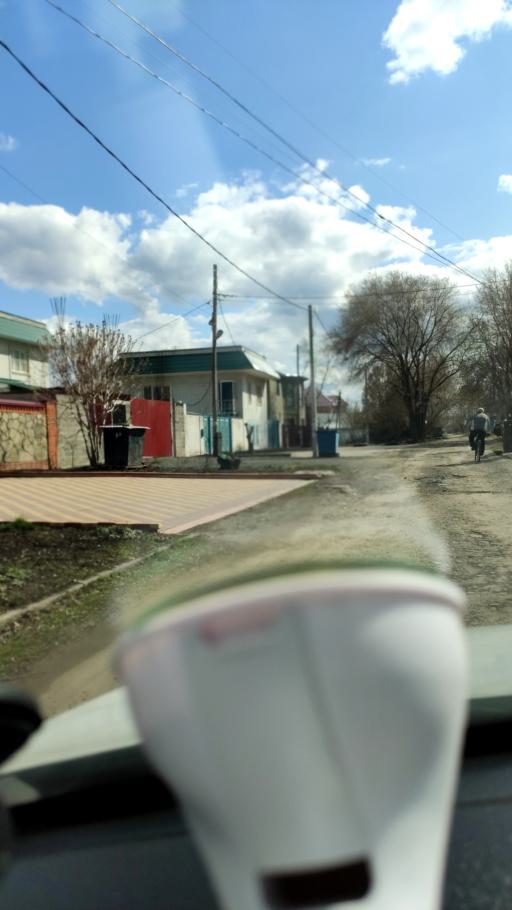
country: RU
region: Samara
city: Petra-Dubrava
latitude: 53.2538
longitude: 50.3338
